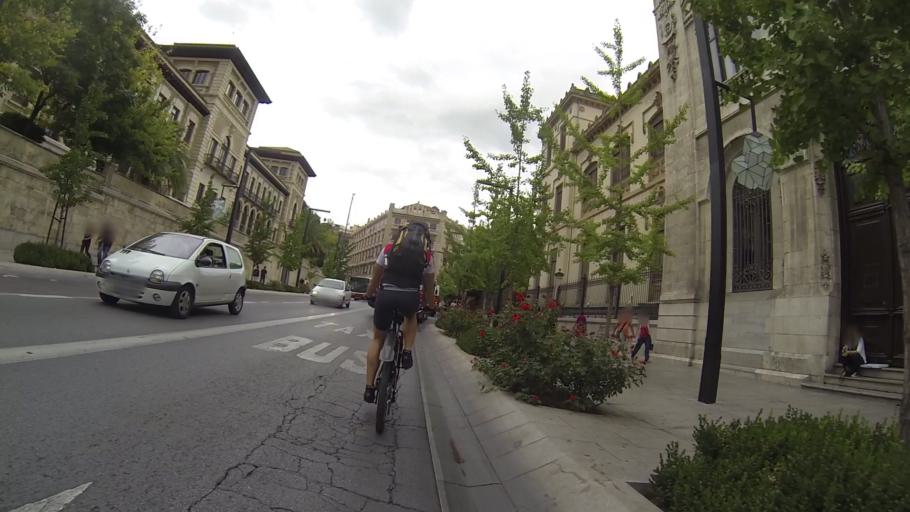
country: ES
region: Andalusia
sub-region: Provincia de Granada
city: Granada
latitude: 37.1827
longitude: -3.6018
